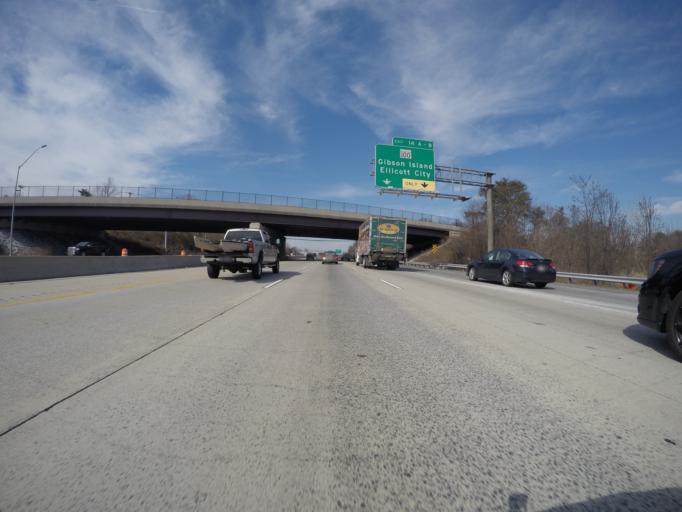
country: US
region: Maryland
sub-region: Anne Arundel County
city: South Gate
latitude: 39.1427
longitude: -76.6443
